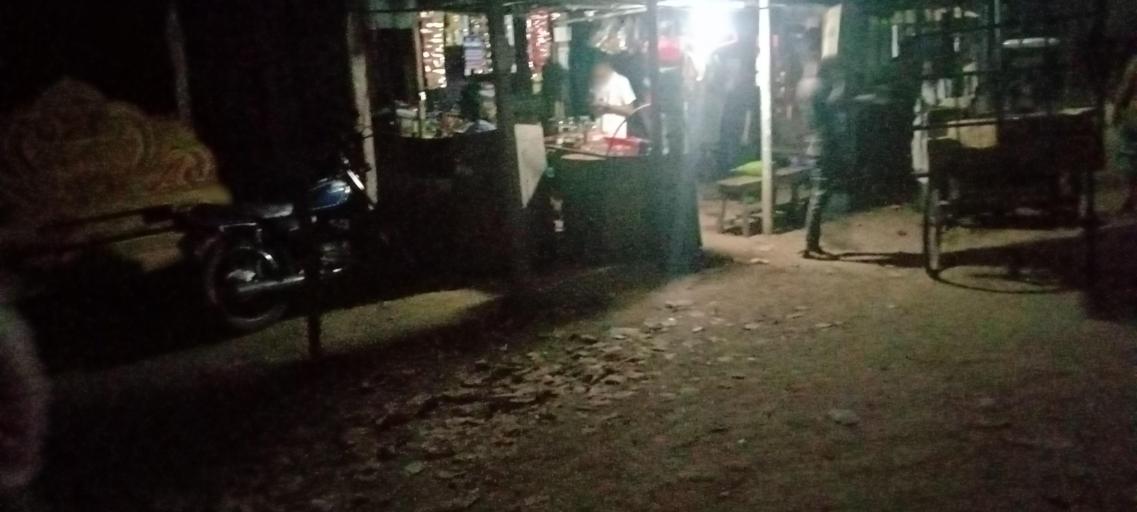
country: BD
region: Dhaka
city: Sakhipur
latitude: 24.3423
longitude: 90.3408
